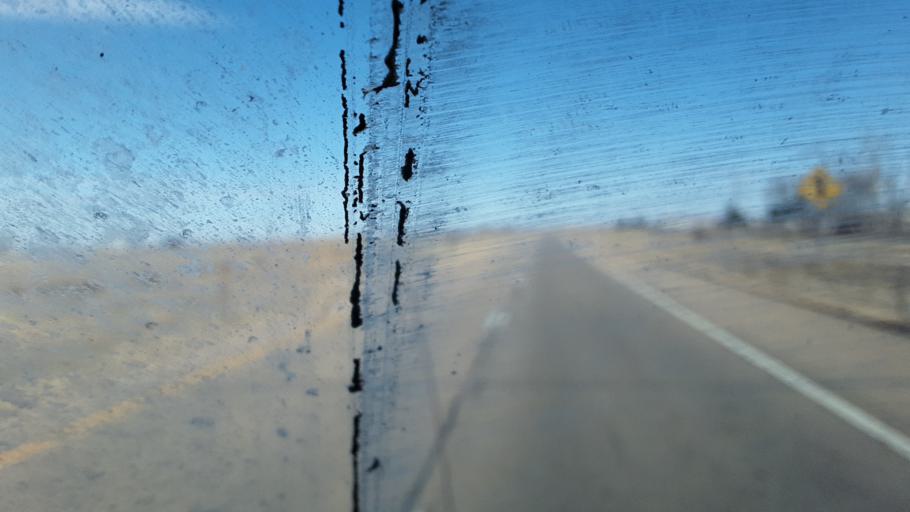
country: US
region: Colorado
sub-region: Weld County
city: Keenesburg
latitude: 40.1705
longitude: -104.3729
